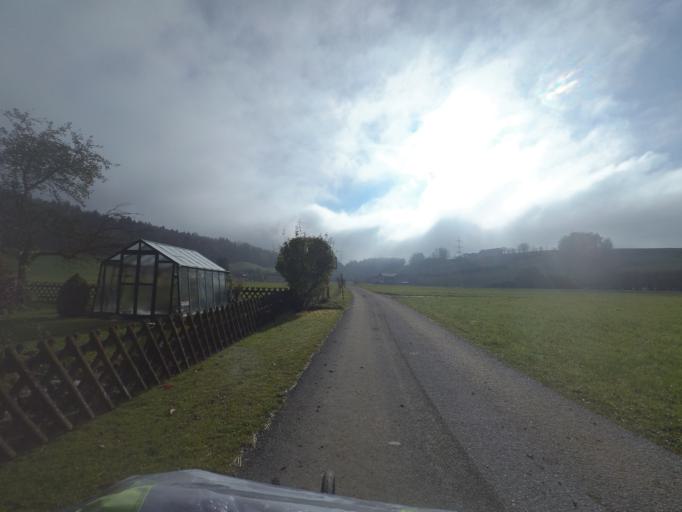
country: AT
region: Salzburg
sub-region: Politischer Bezirk Hallein
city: Adnet
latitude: 47.6806
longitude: 13.1444
